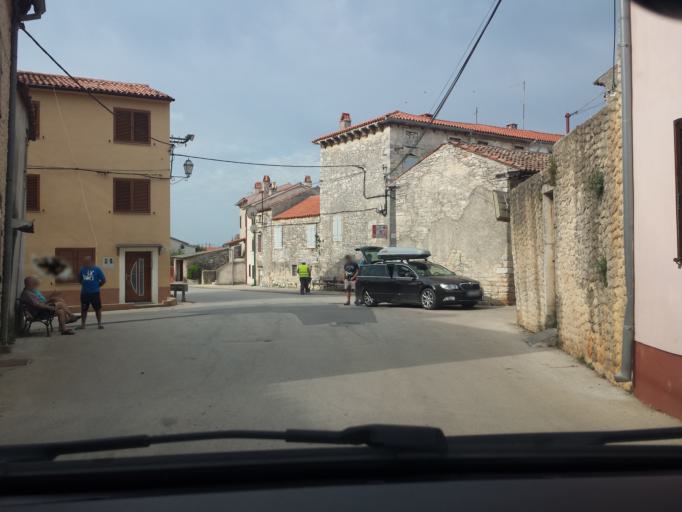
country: HR
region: Istarska
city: Galizana
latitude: 44.9326
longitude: 13.8693
